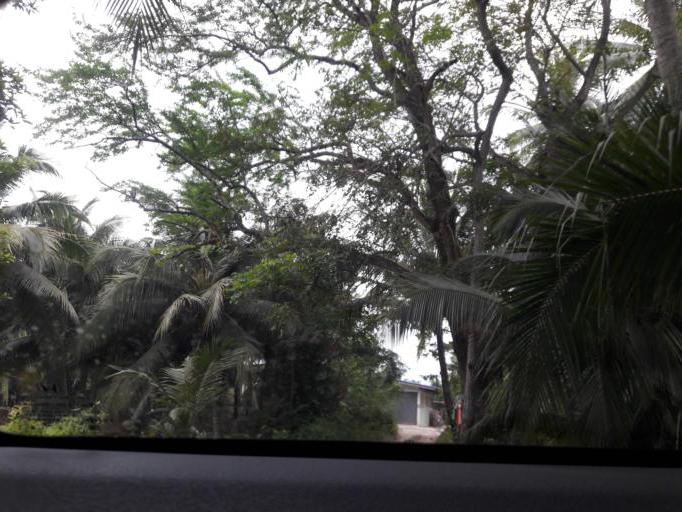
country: TH
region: Ratchaburi
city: Damnoen Saduak
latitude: 13.5665
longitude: 99.9978
